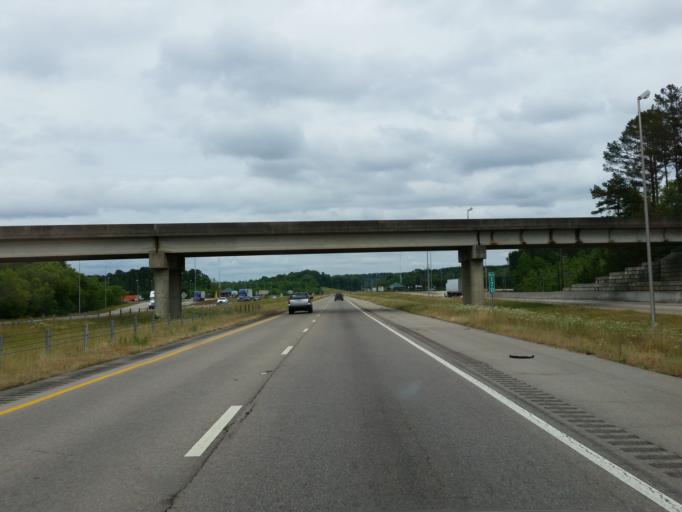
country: US
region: Alabama
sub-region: Sumter County
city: York
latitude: 32.4352
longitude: -88.4406
